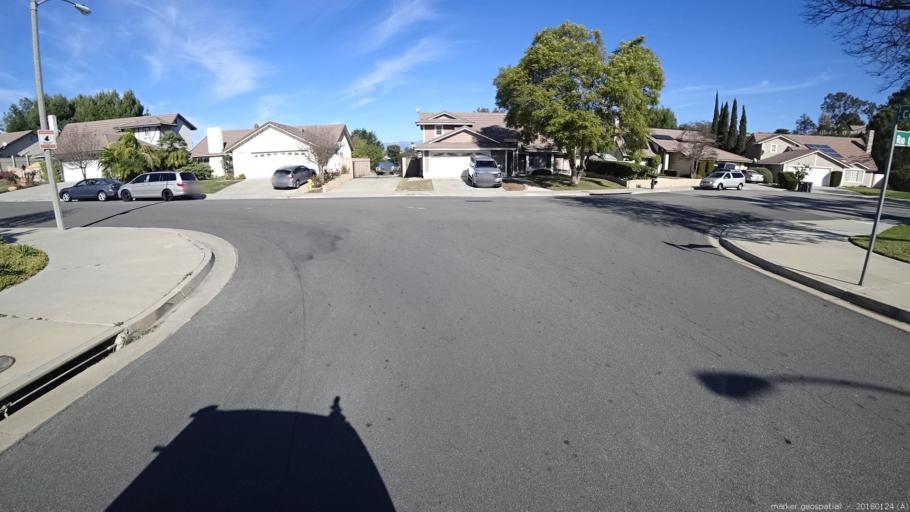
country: US
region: California
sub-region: Los Angeles County
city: Diamond Bar
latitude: 34.0050
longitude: -117.8096
